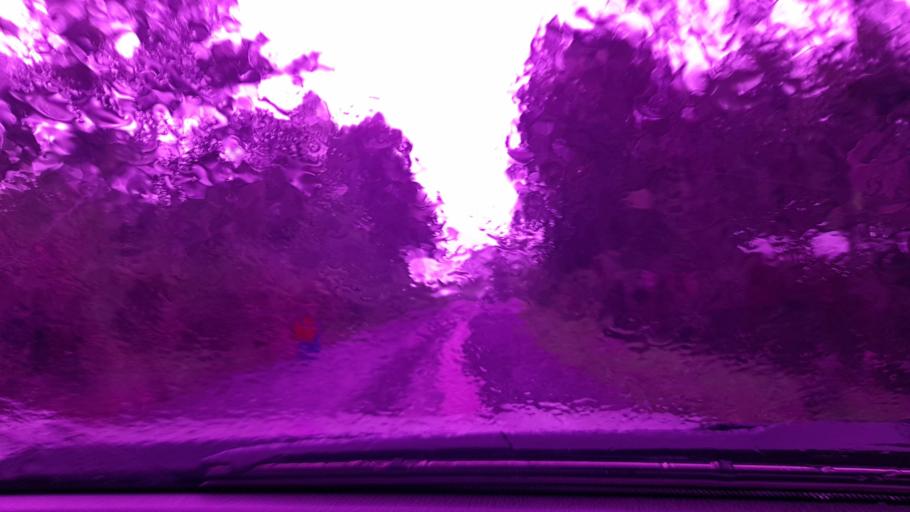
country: ET
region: Oromiya
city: Metu
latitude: 8.3718
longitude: 35.5987
